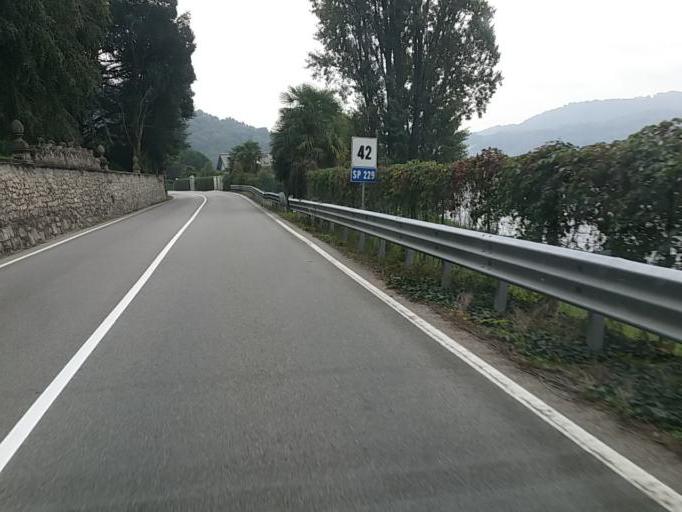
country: IT
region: Piedmont
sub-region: Provincia di Novara
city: Ameno
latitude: 45.7807
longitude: 8.4261
